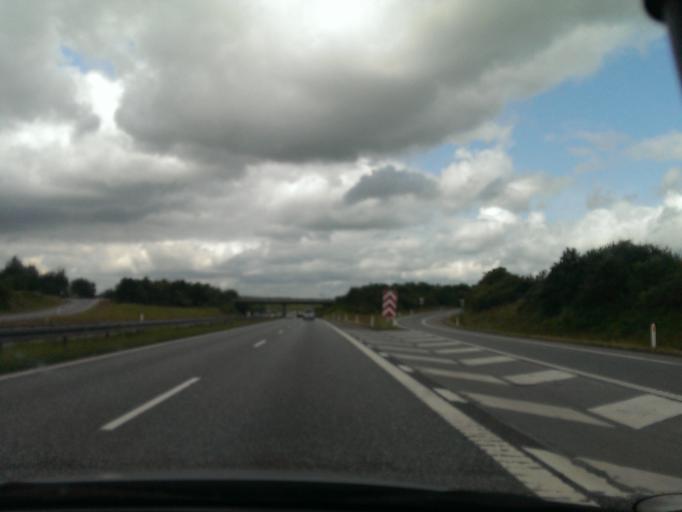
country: DK
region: North Denmark
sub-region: Mariagerfjord Kommune
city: Hobro
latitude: 56.5797
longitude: 9.8162
